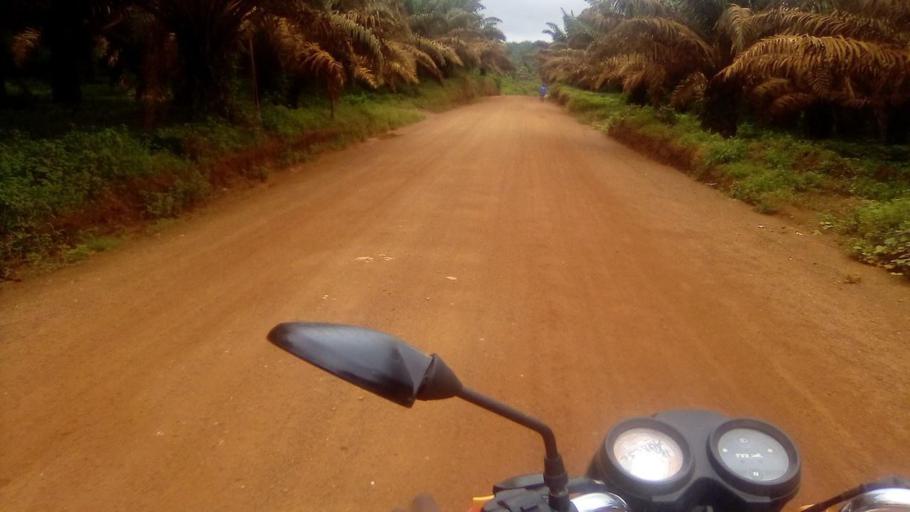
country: SL
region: Southern Province
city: Tongole
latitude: 7.4324
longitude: -11.8522
